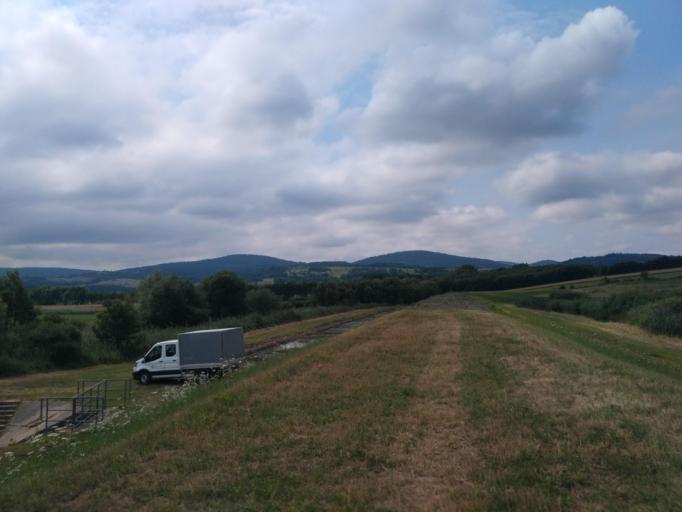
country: PL
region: Subcarpathian Voivodeship
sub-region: Powiat krosnienski
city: Rymanow
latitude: 49.5946
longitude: 21.8446
